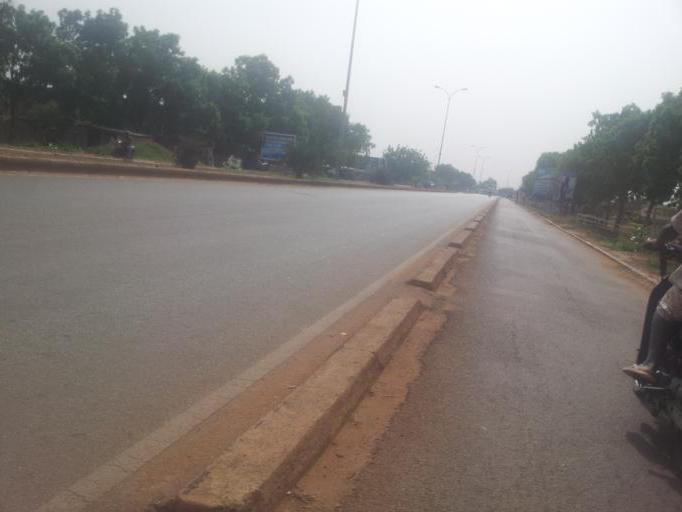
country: BF
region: Centre
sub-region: Kadiogo Province
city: Ouagadougou
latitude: 12.3742
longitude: -1.4981
